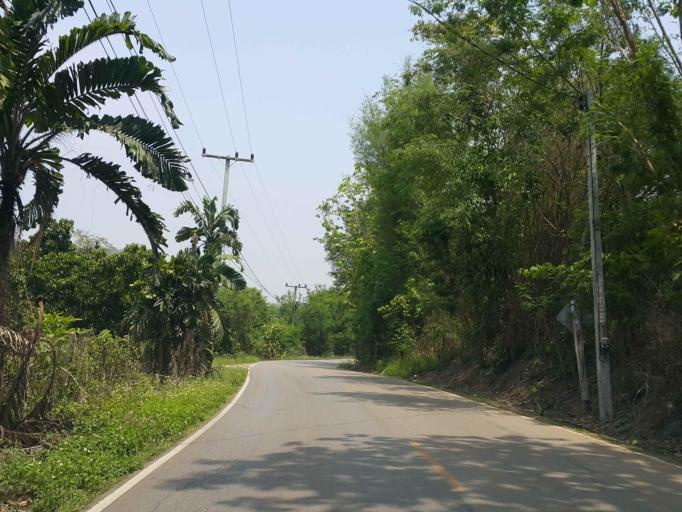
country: TH
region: Chiang Mai
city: Mae Taeng
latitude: 19.0979
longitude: 98.9006
